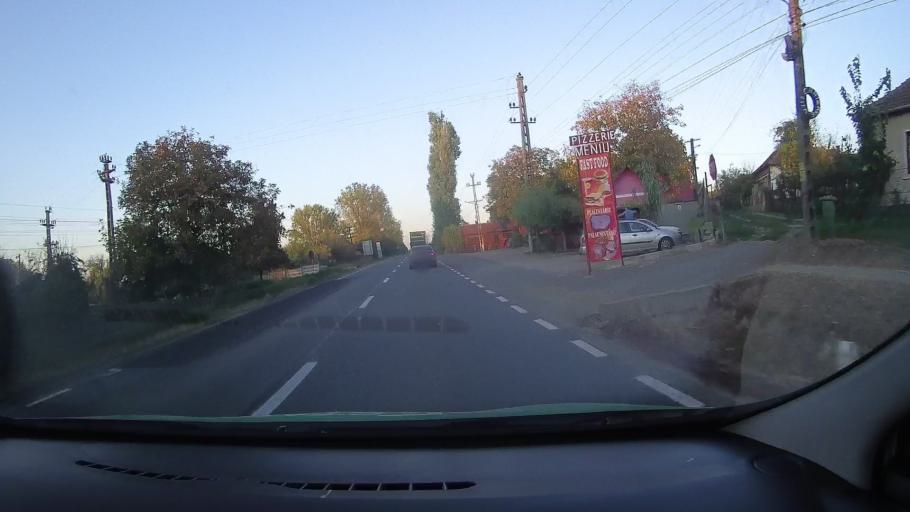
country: RO
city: Dioszeg
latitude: 47.2968
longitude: 22.0130
